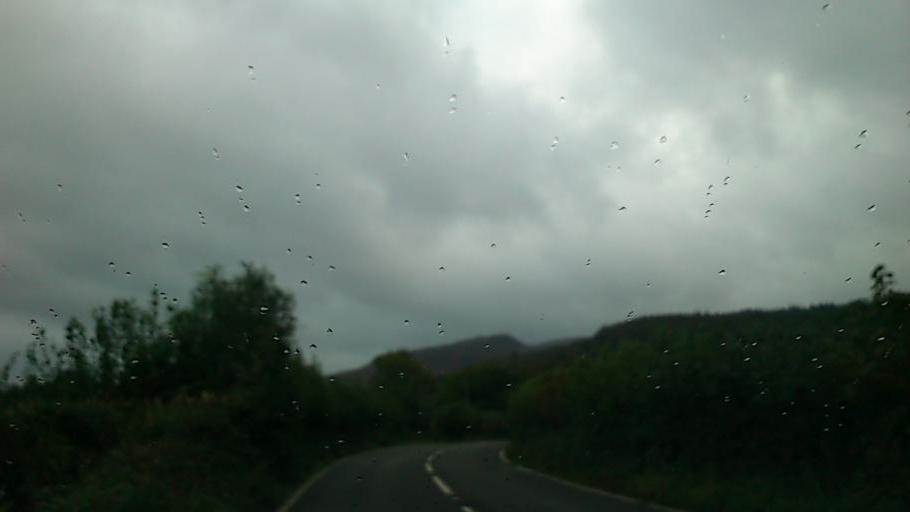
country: GB
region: Wales
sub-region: County of Ceredigion
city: Bow Street
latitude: 52.5291
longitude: -3.9577
